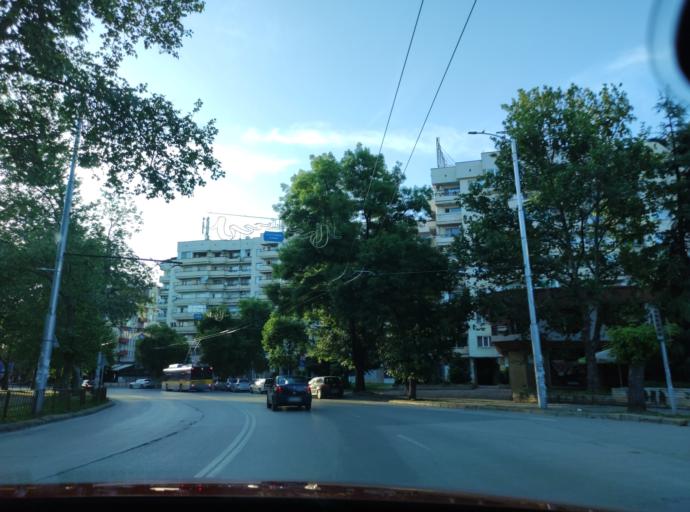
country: BG
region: Pleven
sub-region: Obshtina Pleven
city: Pleven
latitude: 43.4127
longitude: 24.6187
